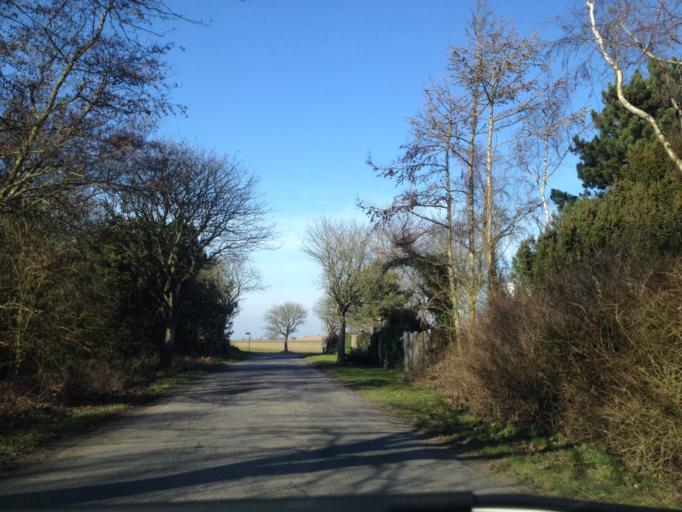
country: DK
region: South Denmark
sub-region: Kerteminde Kommune
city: Munkebo
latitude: 55.5550
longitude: 10.6148
